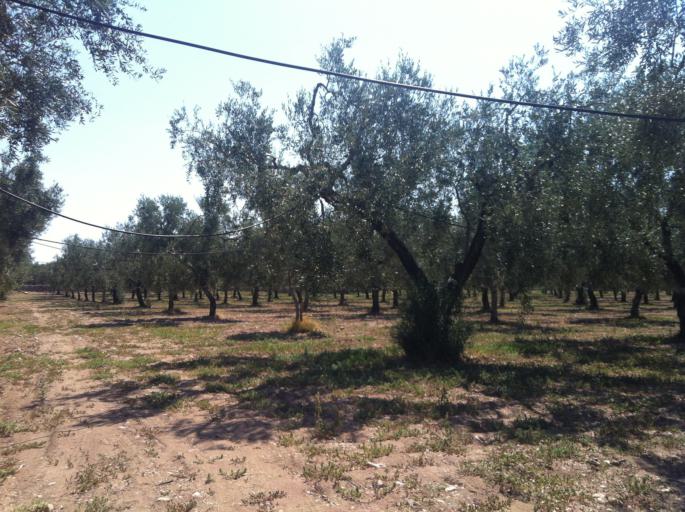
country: IT
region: Apulia
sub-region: Provincia di Foggia
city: Monte Sant'Angelo
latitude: 41.6619
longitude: 15.9518
